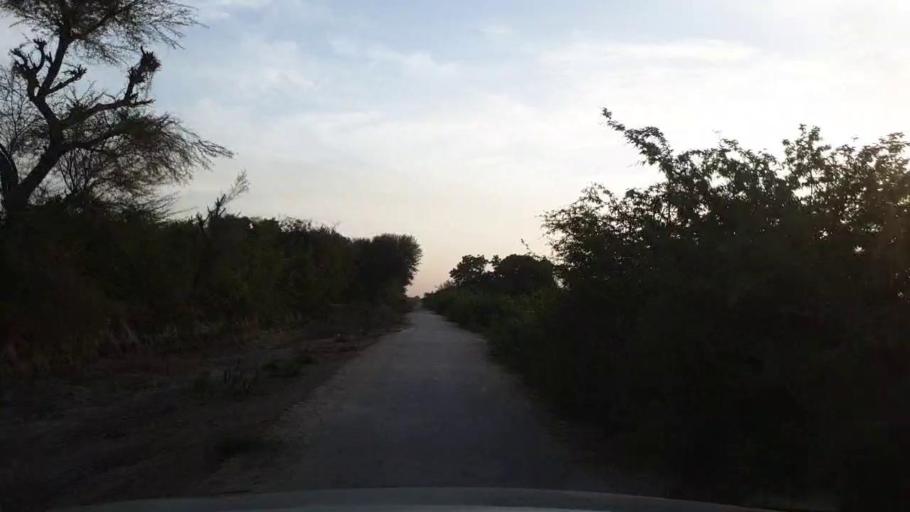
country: PK
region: Sindh
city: Kunri
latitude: 25.1028
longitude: 69.5577
